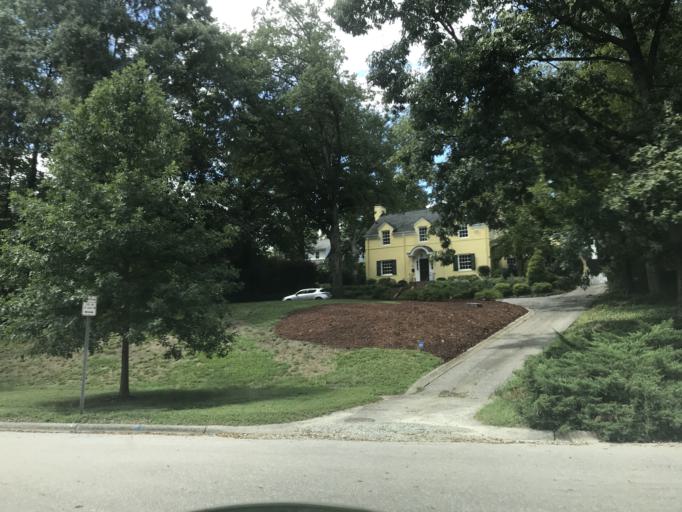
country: US
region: North Carolina
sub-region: Durham County
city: Durham
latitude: 35.9839
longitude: -78.9124
